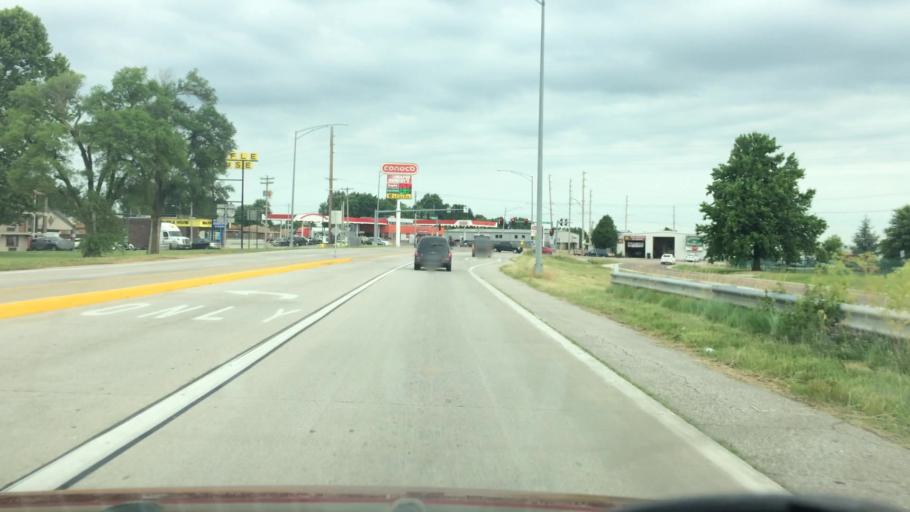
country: US
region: Missouri
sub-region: Greene County
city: Springfield
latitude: 37.2529
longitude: -93.2642
